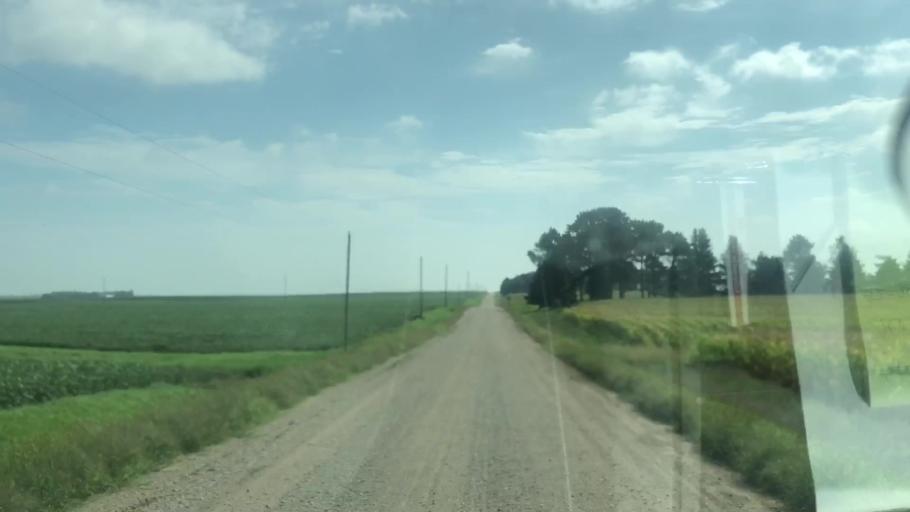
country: US
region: Iowa
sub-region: Lyon County
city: George
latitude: 43.2153
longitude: -95.9873
